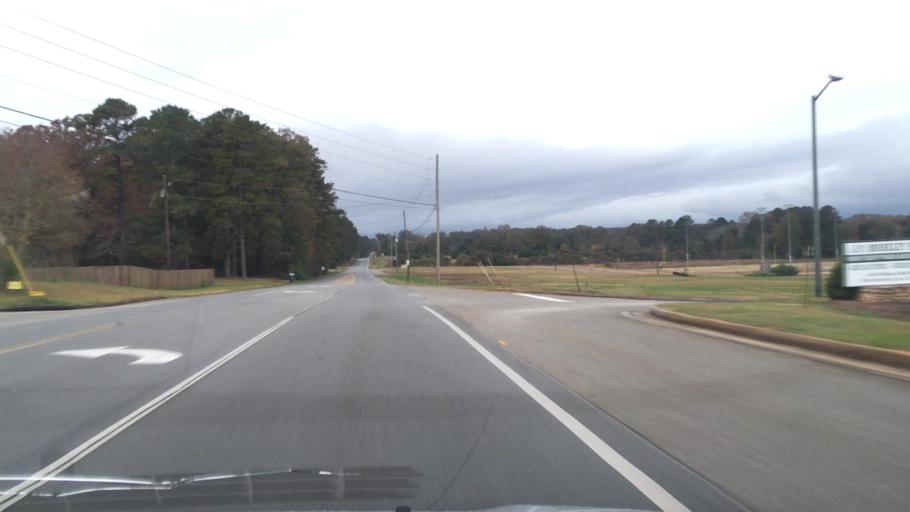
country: US
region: Georgia
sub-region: Henry County
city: Stockbridge
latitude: 33.5320
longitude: -84.1631
